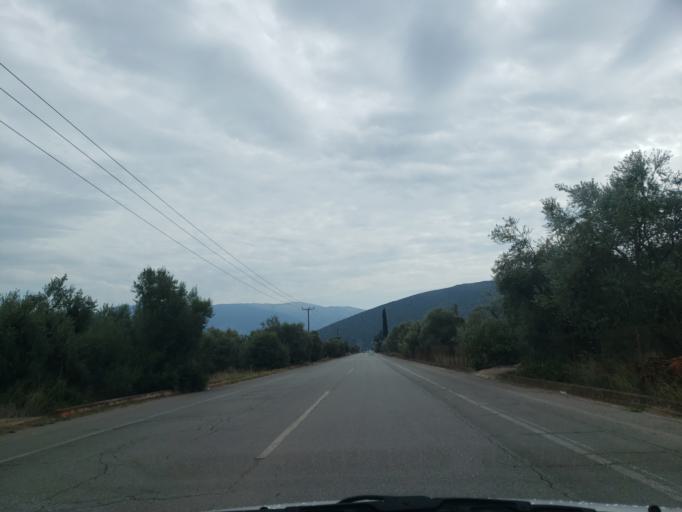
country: GR
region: Central Greece
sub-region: Nomos Fokidos
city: Amfissa
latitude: 38.4960
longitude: 22.4112
